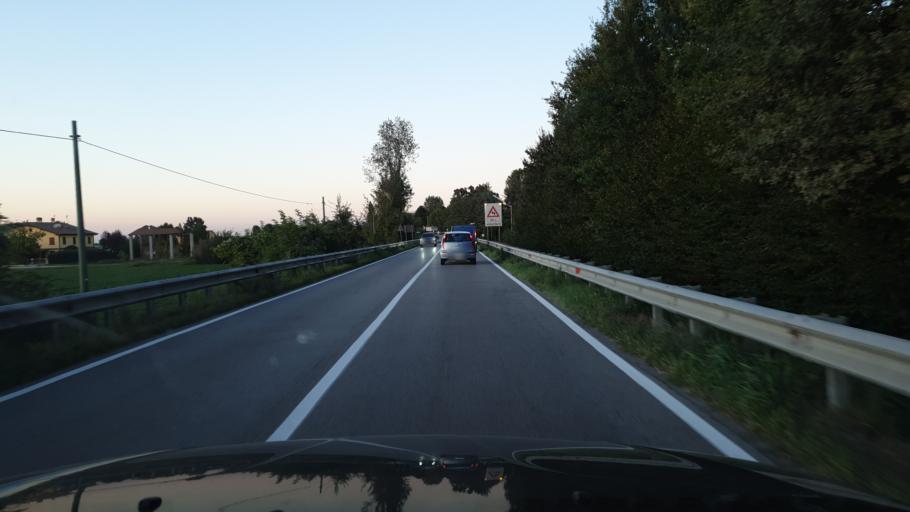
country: IT
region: Emilia-Romagna
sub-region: Provincia di Bologna
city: Ca De Fabbri
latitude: 44.5962
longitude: 11.4366
